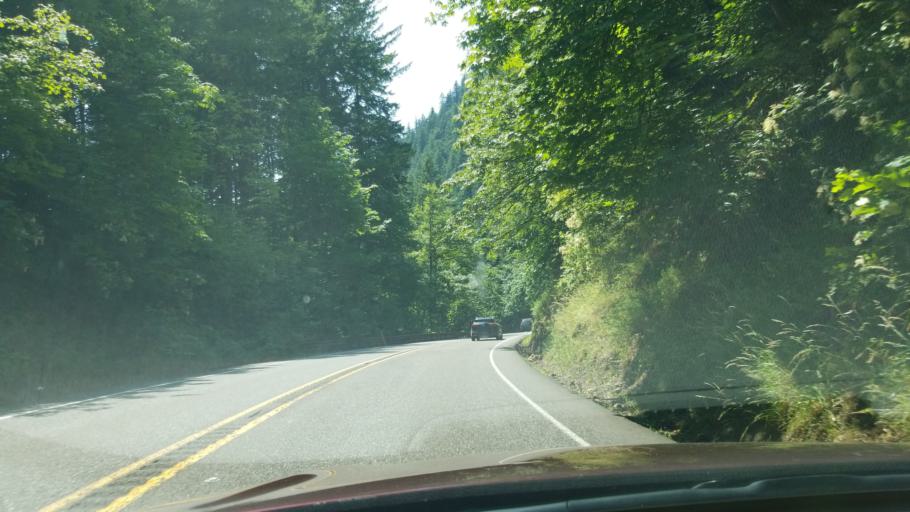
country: US
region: Washington
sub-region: Clark County
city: Washougal
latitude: 45.5857
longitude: -122.1901
